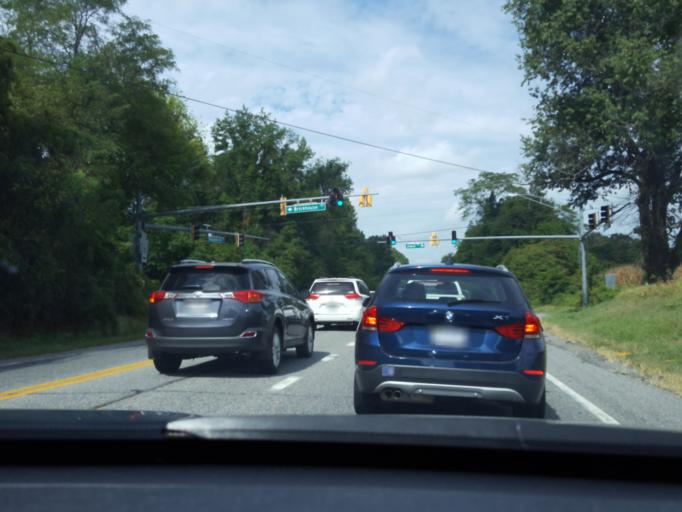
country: US
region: Maryland
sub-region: Calvert County
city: Dunkirk Town Center
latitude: 38.7483
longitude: -76.6392
